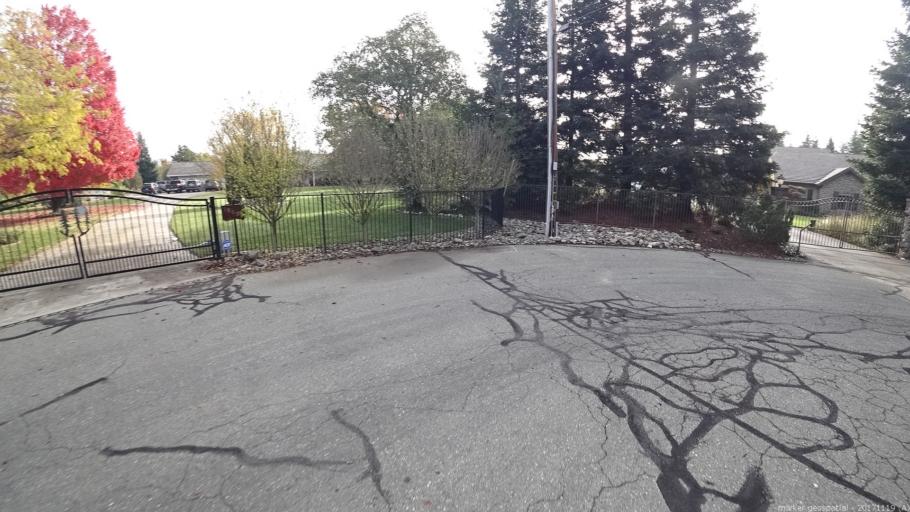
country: US
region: California
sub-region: Shasta County
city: Anderson
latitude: 40.5094
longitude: -122.3264
